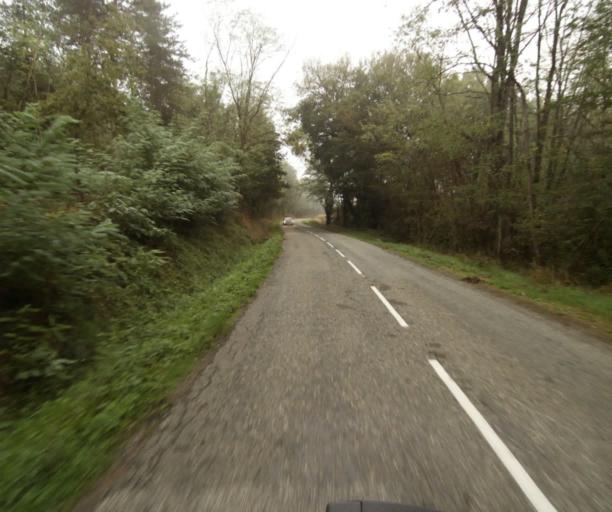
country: FR
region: Midi-Pyrenees
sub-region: Departement du Tarn-et-Garonne
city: Saint-Nauphary
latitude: 43.9380
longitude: 1.4611
